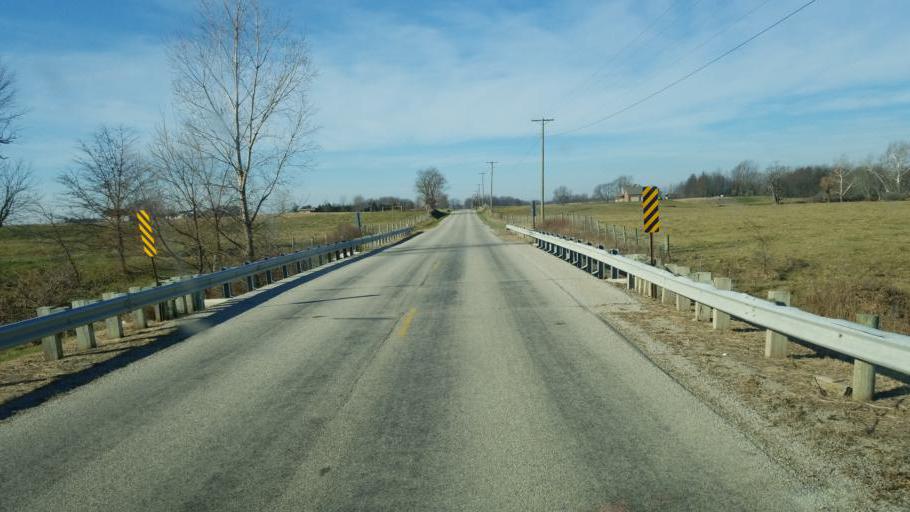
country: US
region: Ohio
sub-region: Richland County
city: Shelby
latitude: 40.8432
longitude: -82.6528
